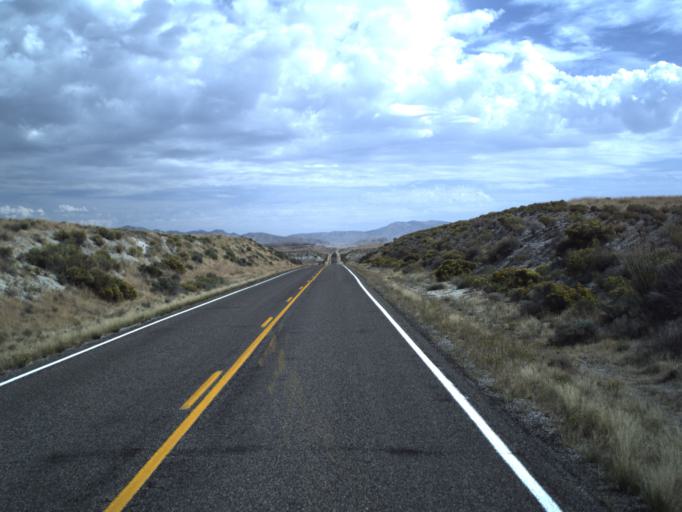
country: US
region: Utah
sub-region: Tooele County
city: Wendover
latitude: 41.4033
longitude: -113.9449
